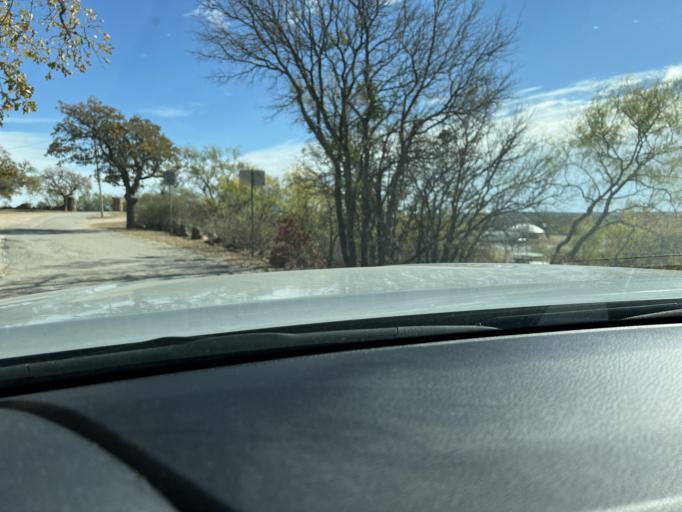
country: US
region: Texas
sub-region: Eastland County
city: Eastland
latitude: 32.3971
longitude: -98.8344
